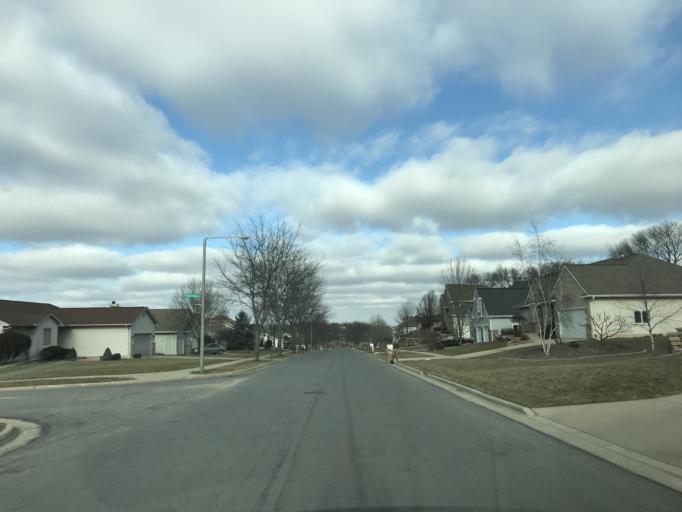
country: US
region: Wisconsin
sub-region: Dane County
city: Monona
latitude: 43.1090
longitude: -89.2913
